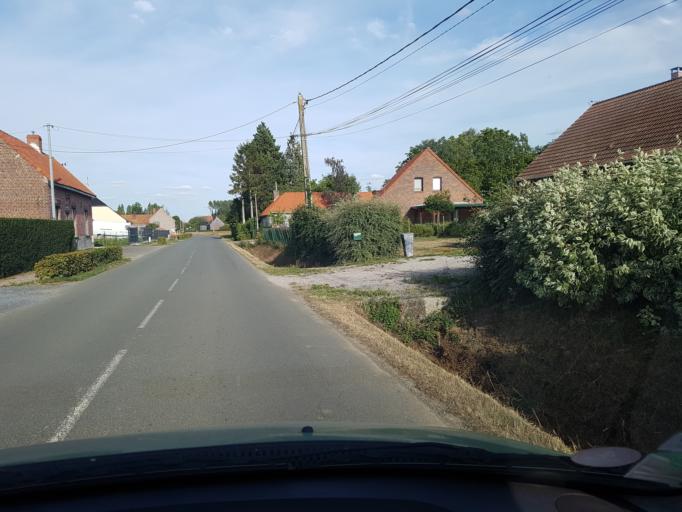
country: FR
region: Nord-Pas-de-Calais
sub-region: Departement du Pas-de-Calais
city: La Couture
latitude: 50.5945
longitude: 2.7200
